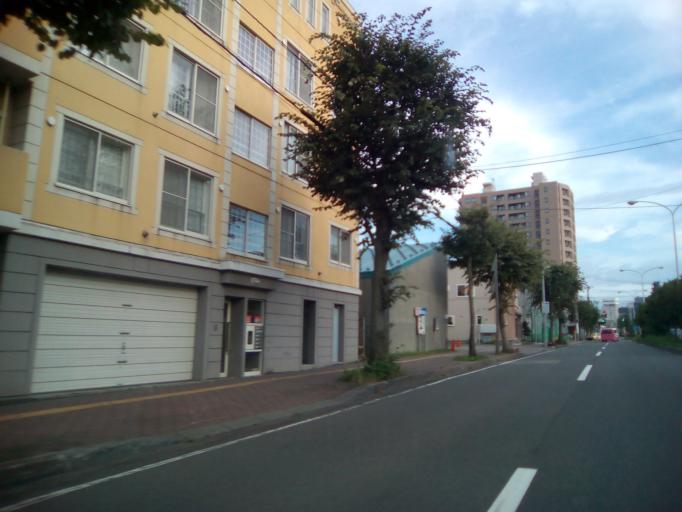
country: JP
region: Hokkaido
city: Sapporo
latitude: 43.0441
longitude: 141.3699
